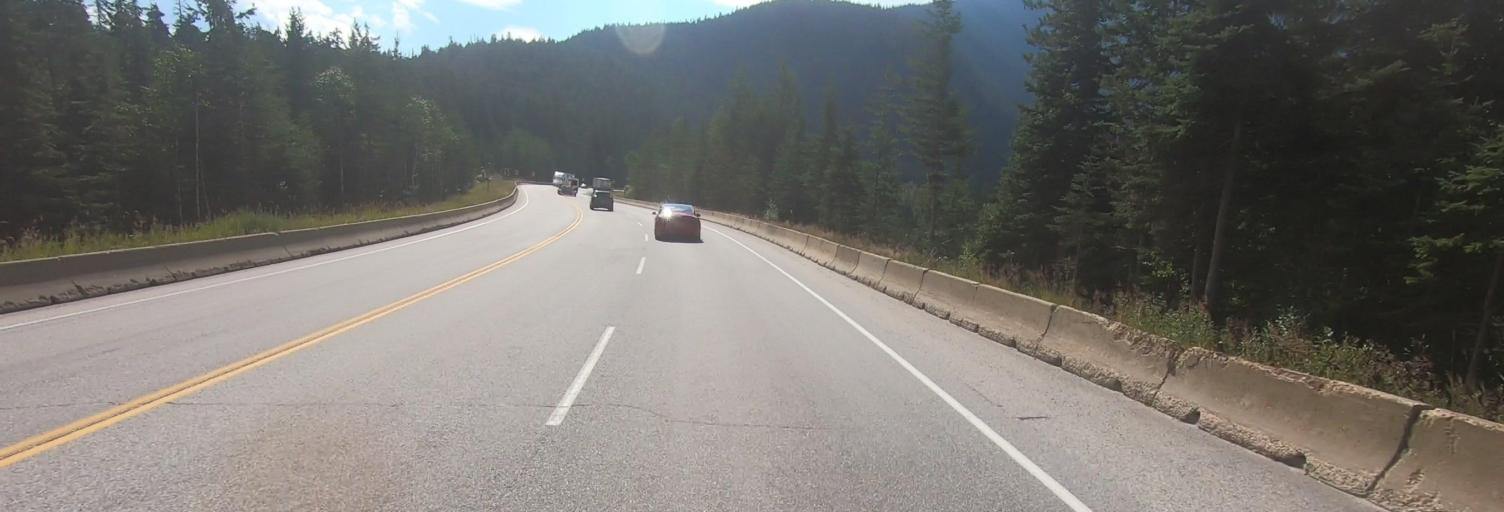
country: CA
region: British Columbia
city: Golden
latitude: 51.3484
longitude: -117.4358
